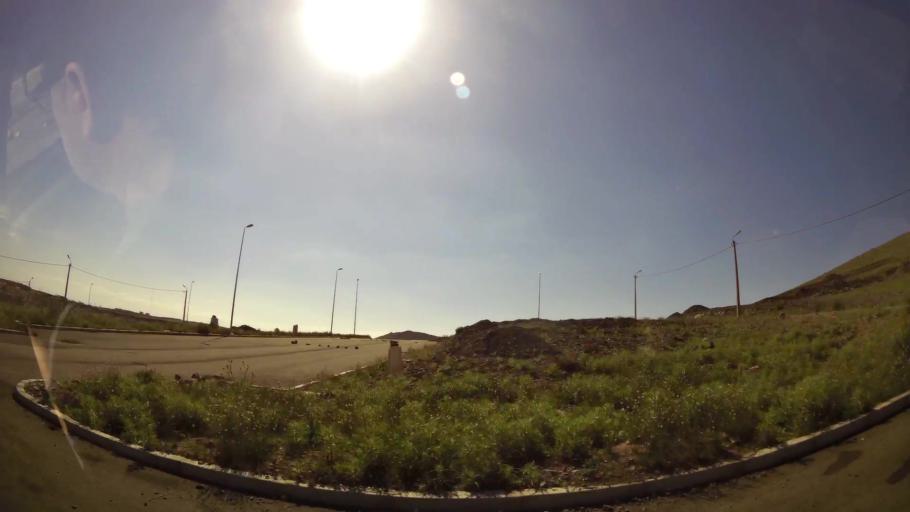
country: MA
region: Oriental
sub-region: Oujda-Angad
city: Oujda
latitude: 34.6478
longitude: -1.9571
